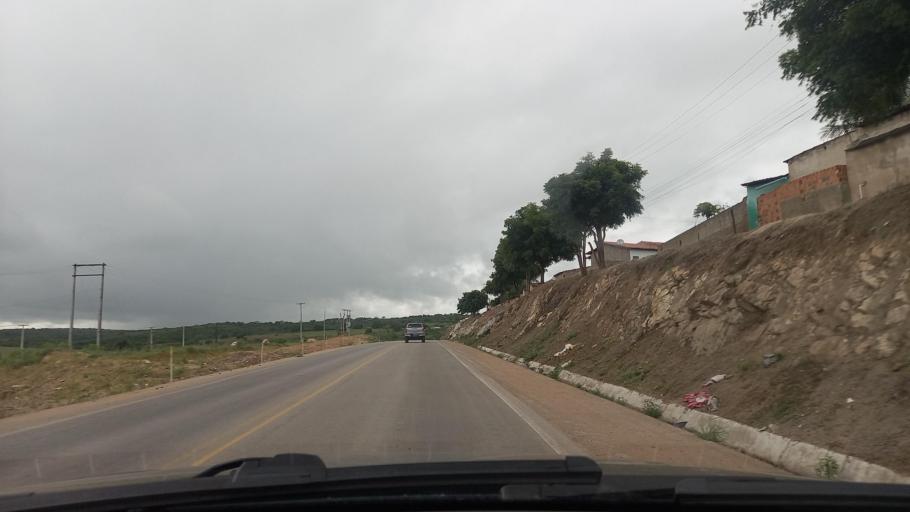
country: BR
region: Alagoas
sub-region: Batalha
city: Batalha
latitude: -9.6313
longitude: -37.2063
